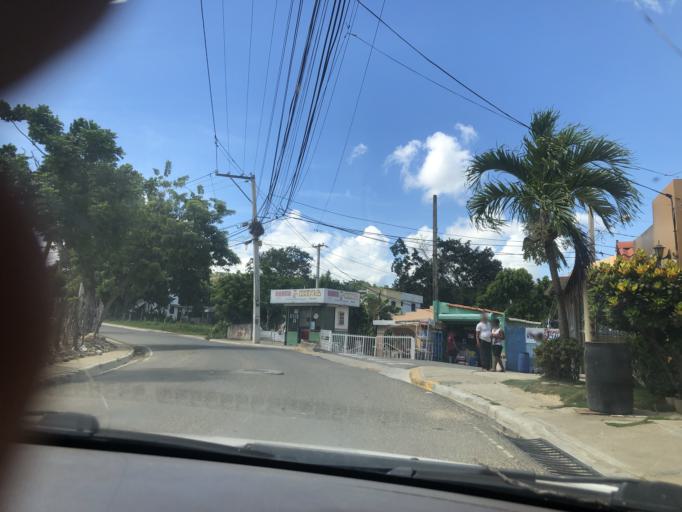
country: DO
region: Santiago
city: Santiago de los Caballeros
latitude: 19.4112
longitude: -70.7094
